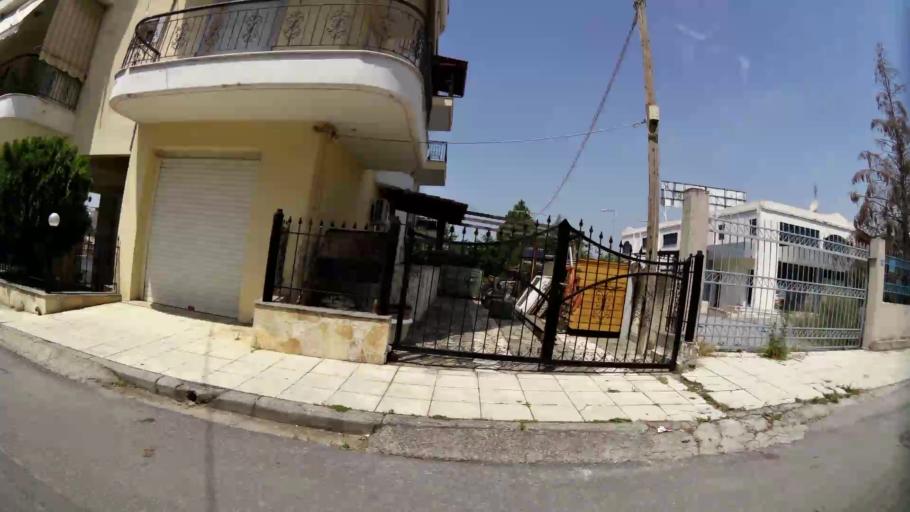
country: GR
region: Central Macedonia
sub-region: Nomos Thessalonikis
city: Evosmos
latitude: 40.6757
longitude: 22.8948
